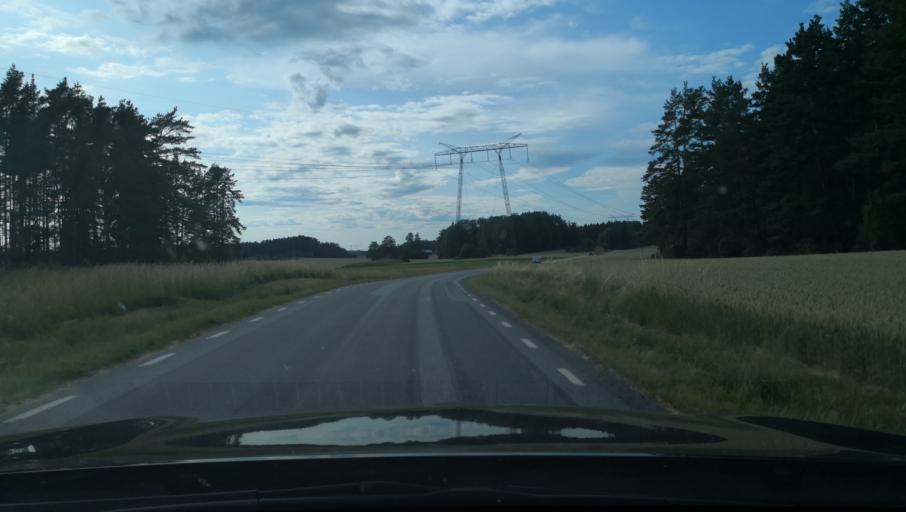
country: SE
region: Uppsala
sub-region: Enkopings Kommun
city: Orsundsbro
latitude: 59.6761
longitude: 17.4179
